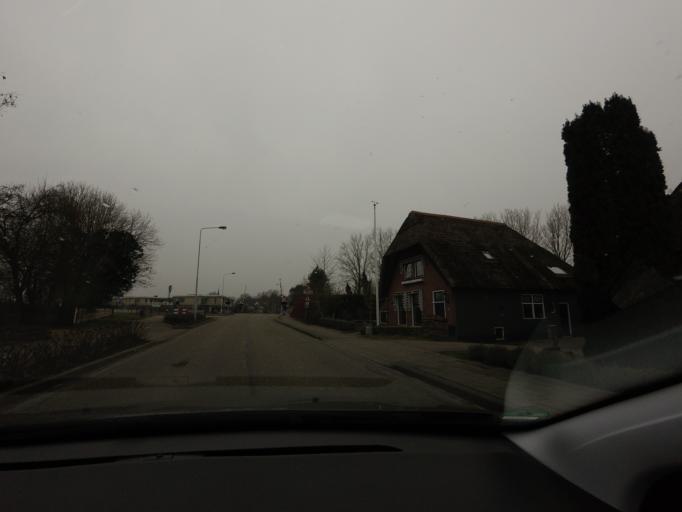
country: NL
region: Friesland
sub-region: Gemeente Franekeradeel
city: Franeker
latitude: 53.1820
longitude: 5.5528
